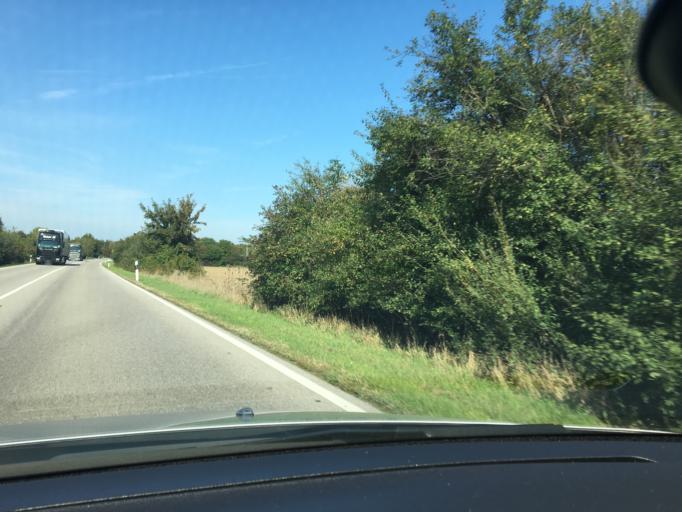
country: DE
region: Bavaria
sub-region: Upper Bavaria
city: Stammham
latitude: 48.3031
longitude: 11.8782
